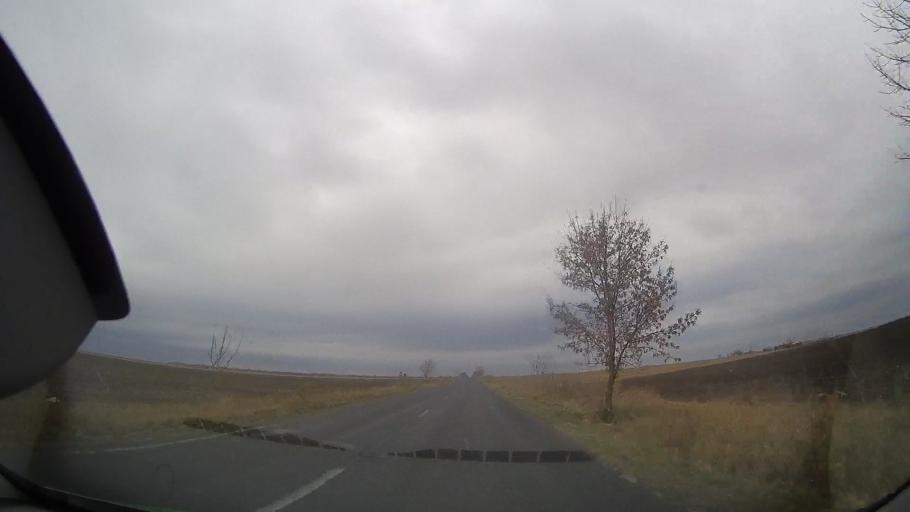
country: RO
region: Buzau
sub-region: Comuna Padina
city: Padina
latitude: 44.7942
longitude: 27.1408
